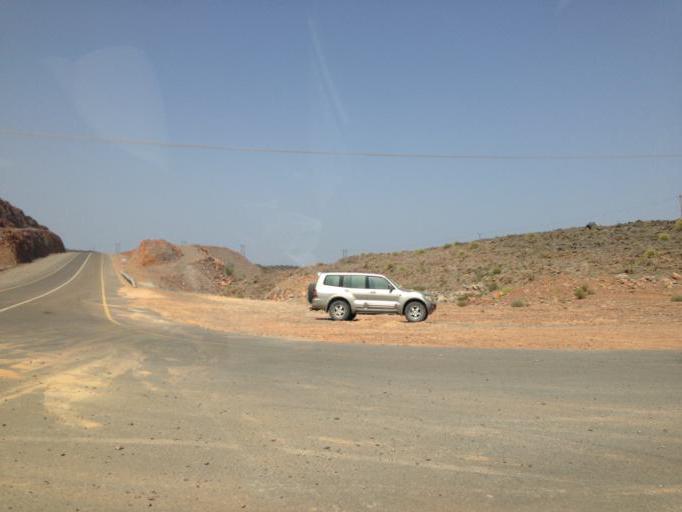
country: OM
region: Ash Sharqiyah
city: Ibra'
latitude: 23.0868
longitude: 58.9506
